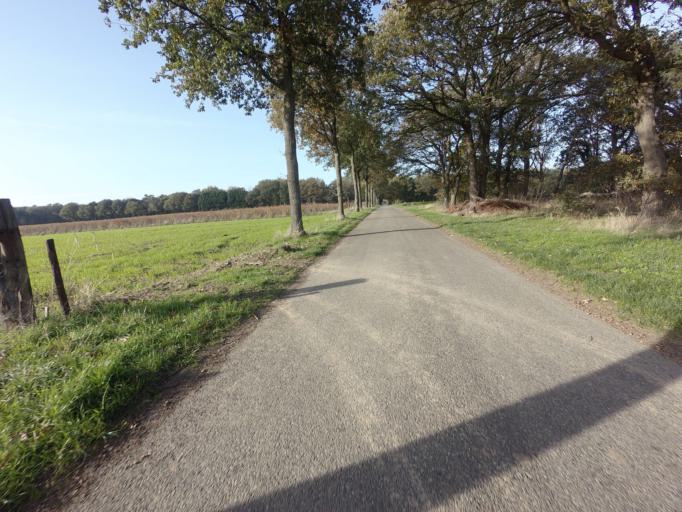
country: NL
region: Limburg
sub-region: Gemeente Echt-Susteren
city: Koningsbosch
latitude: 51.0575
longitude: 5.9308
